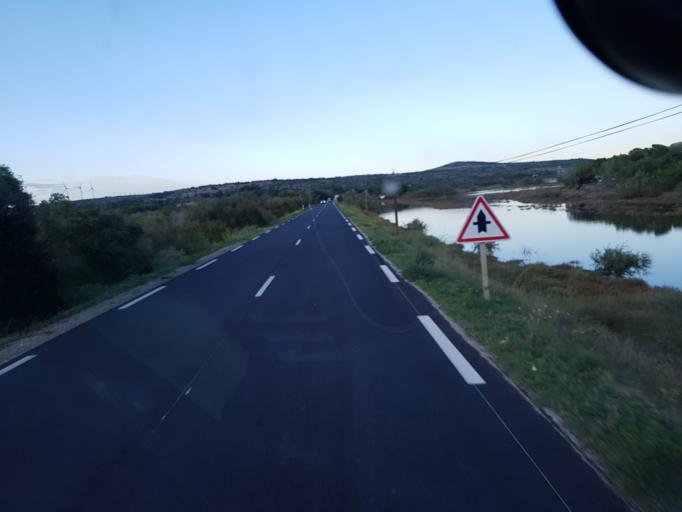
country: FR
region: Languedoc-Roussillon
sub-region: Departement de l'Aude
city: Sigean
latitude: 42.9683
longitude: 2.9985
